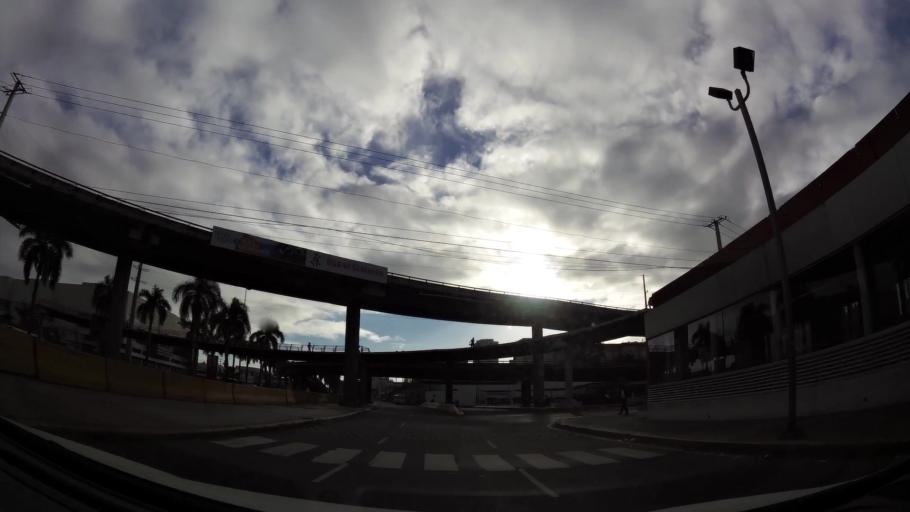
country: DO
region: Nacional
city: La Julia
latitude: 18.4822
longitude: -69.9466
